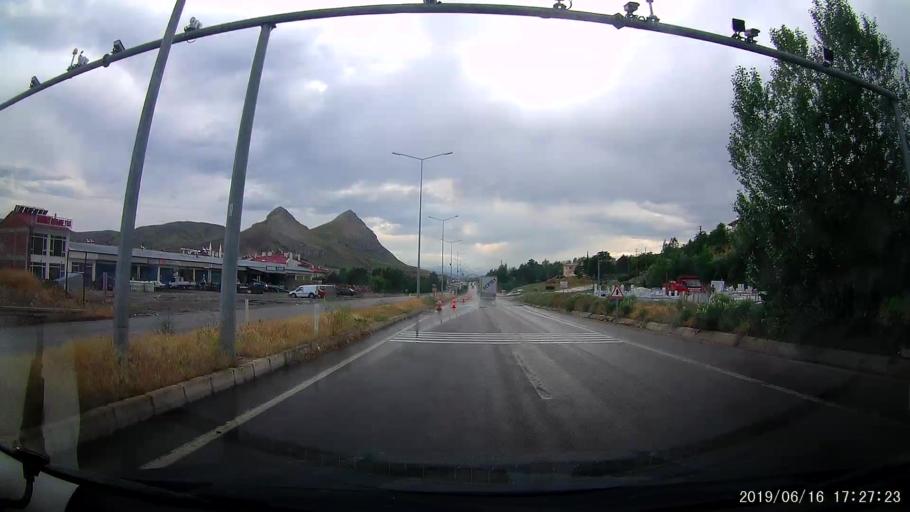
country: TR
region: Erzincan
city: Tercan
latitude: 39.7760
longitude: 40.3941
